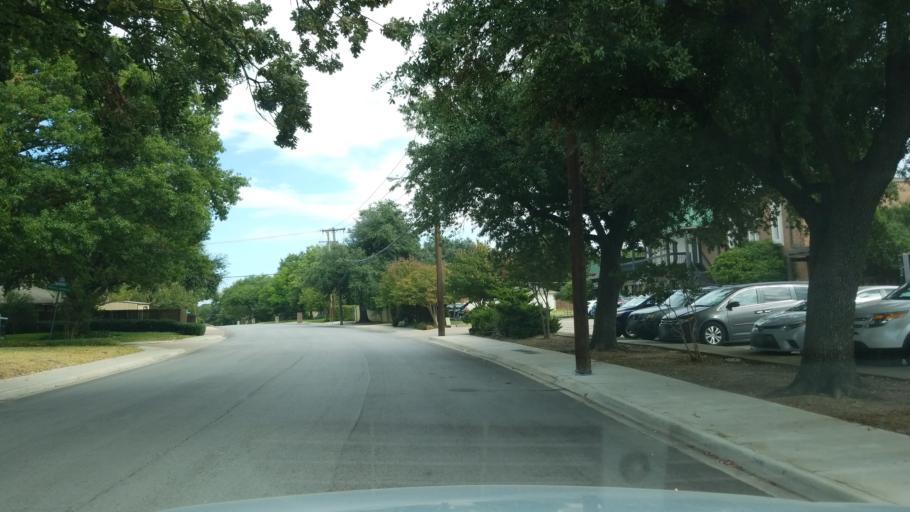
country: US
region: Texas
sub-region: Dallas County
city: Richardson
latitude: 32.9527
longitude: -96.7715
